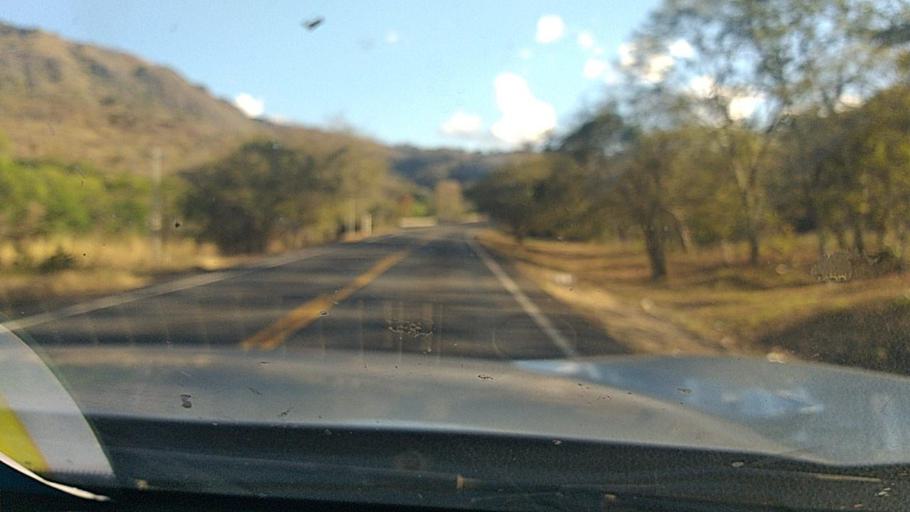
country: NI
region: Esteli
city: Condega
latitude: 13.2854
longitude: -86.3456
